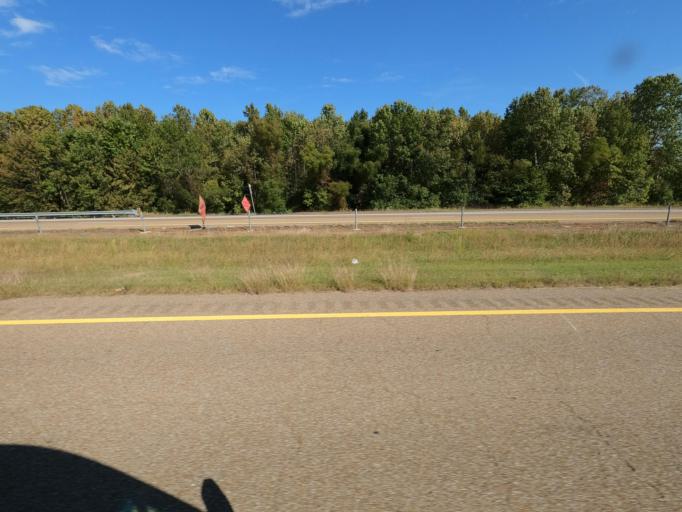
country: US
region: Tennessee
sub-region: Shelby County
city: Millington
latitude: 35.3083
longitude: -89.8321
